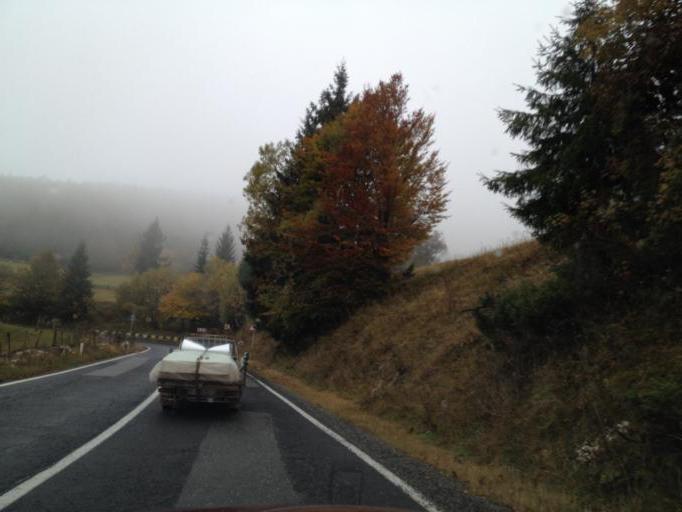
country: RO
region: Brasov
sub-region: Comuna Fundata
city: Fundata
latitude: 45.4460
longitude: 25.2736
